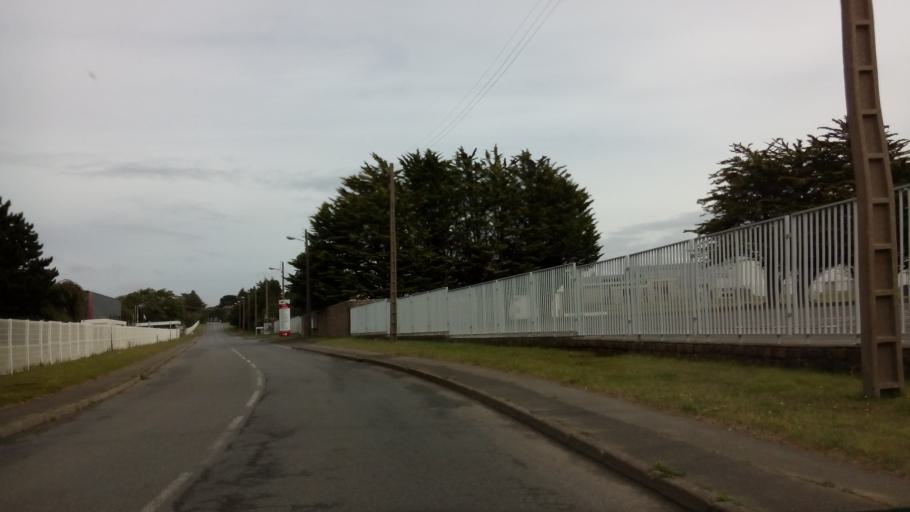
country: FR
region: Brittany
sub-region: Departement des Cotes-d'Armor
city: Lannion
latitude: 48.7576
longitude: -3.4612
